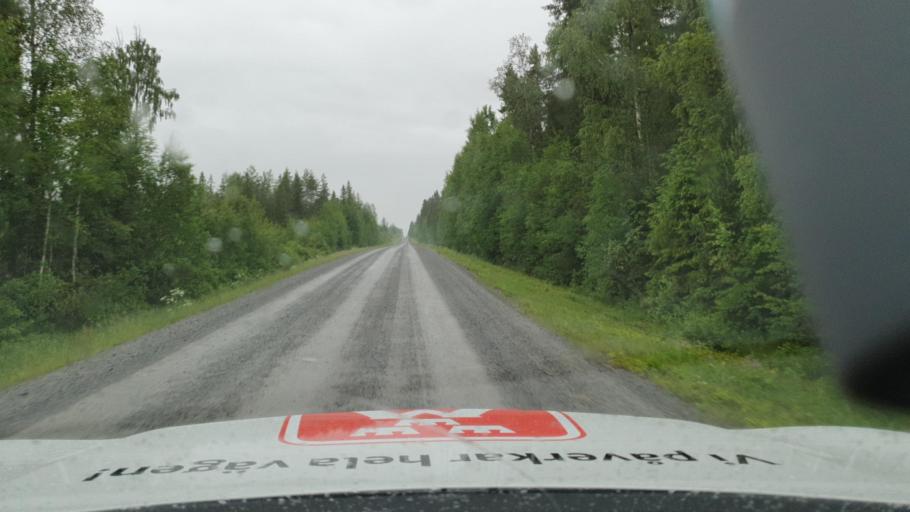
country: SE
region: Vaesterbotten
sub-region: Bjurholms Kommun
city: Bjurholm
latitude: 63.8468
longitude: 19.4780
